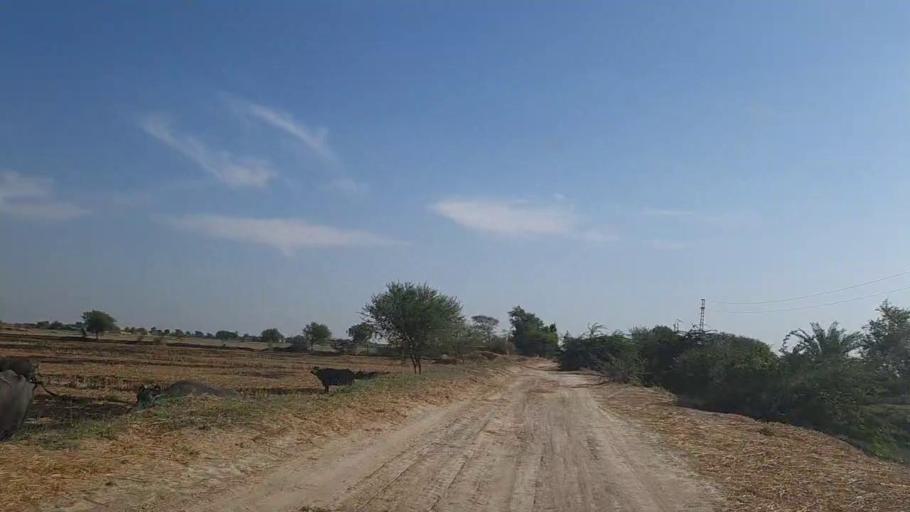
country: PK
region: Sindh
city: Bulri
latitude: 24.8651
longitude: 68.2839
